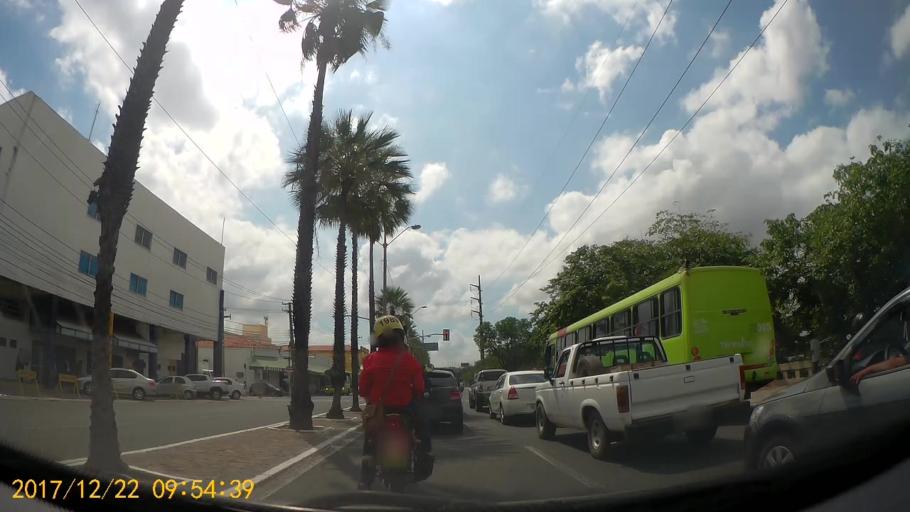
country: BR
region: Piaui
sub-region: Teresina
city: Teresina
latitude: -5.0945
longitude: -42.8176
